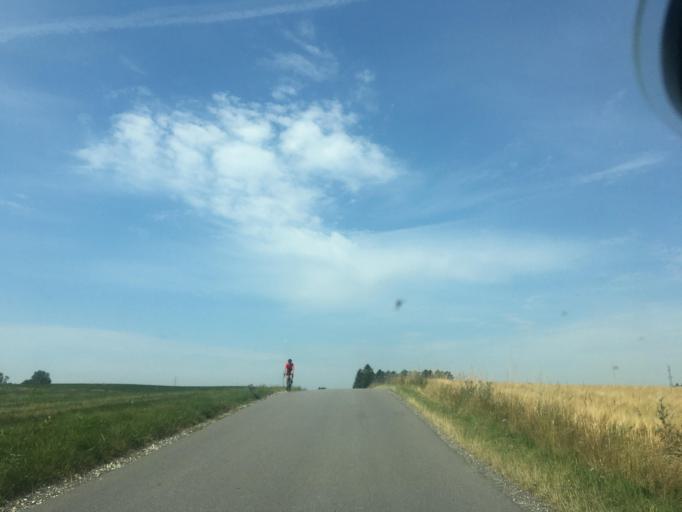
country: DK
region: Zealand
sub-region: Faxe Kommune
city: Ronnede
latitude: 55.2048
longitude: 12.0227
